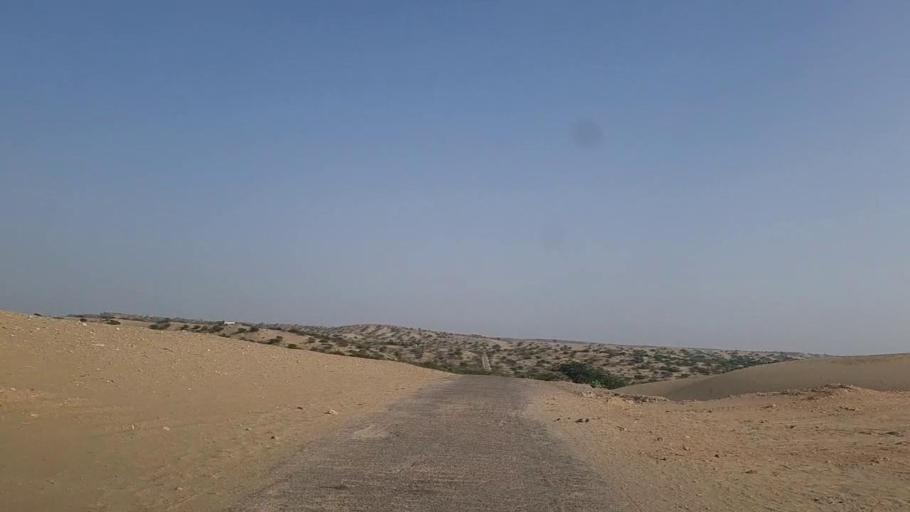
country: PK
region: Sindh
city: Naukot
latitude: 24.6281
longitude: 69.3643
